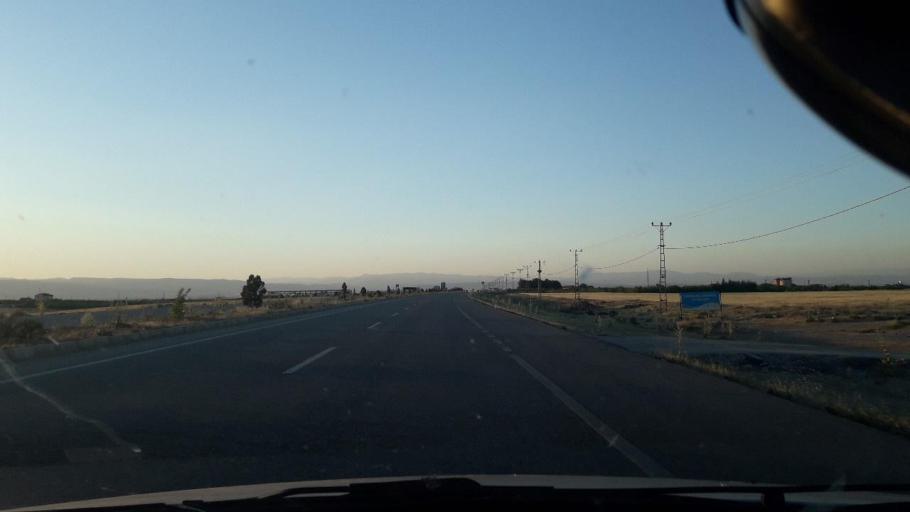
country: TR
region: Malatya
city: Yesilyurt
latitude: 38.3774
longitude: 38.2253
